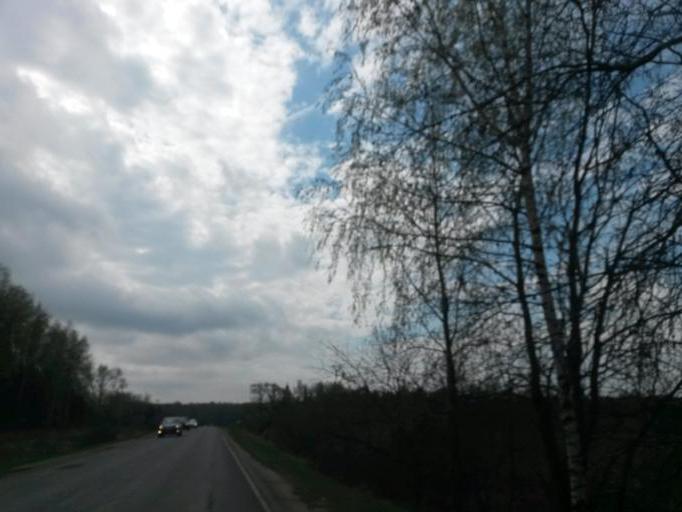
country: RU
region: Moskovskaya
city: L'vovskiy
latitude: 55.3214
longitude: 37.6115
